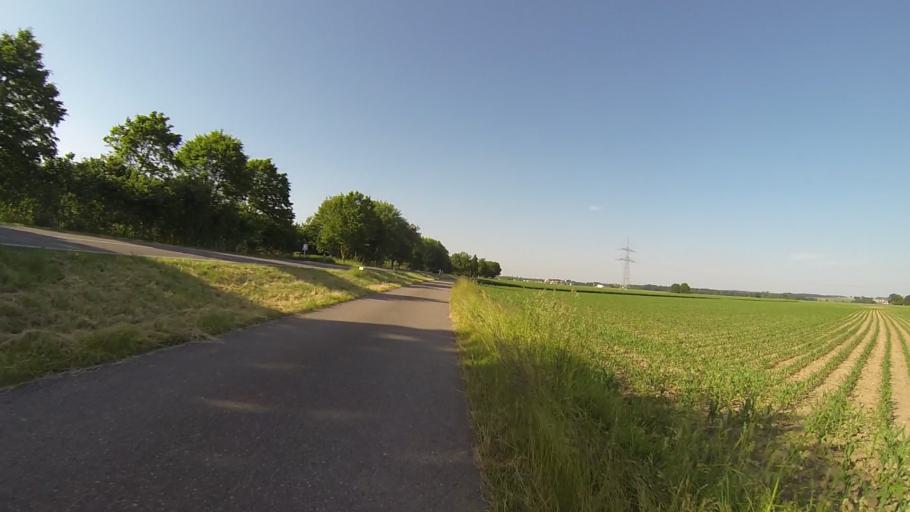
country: DE
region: Baden-Wuerttemberg
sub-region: Tuebingen Region
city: Mietingen
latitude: 48.1842
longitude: 9.8688
